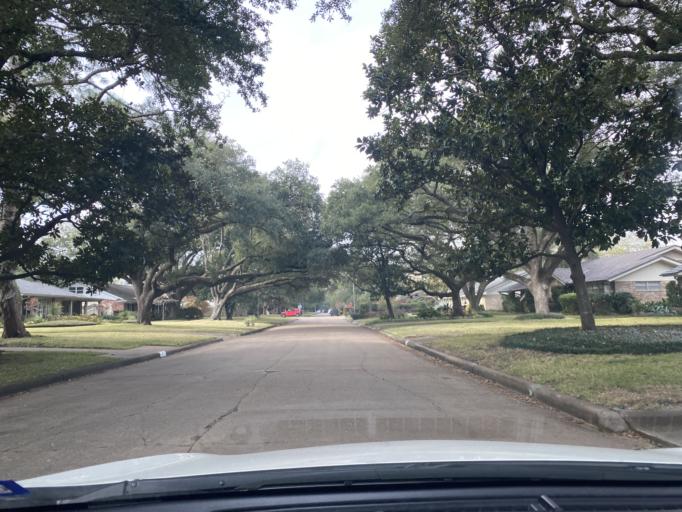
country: US
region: Texas
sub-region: Harris County
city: Hunters Creek Village
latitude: 29.7663
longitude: -95.4770
